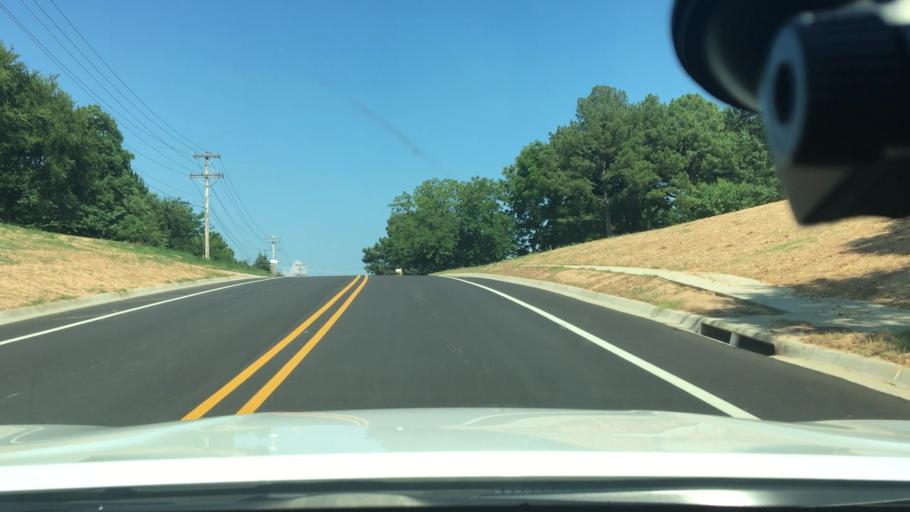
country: US
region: Arkansas
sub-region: Johnson County
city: Clarksville
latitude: 35.4619
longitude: -93.4950
